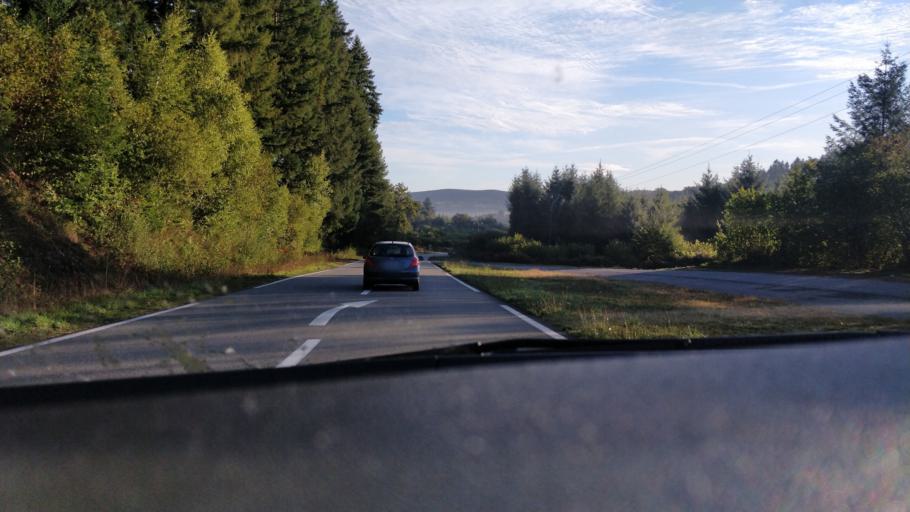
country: FR
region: Limousin
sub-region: Departement de la Creuse
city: Bourganeuf
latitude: 45.9506
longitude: 1.7199
